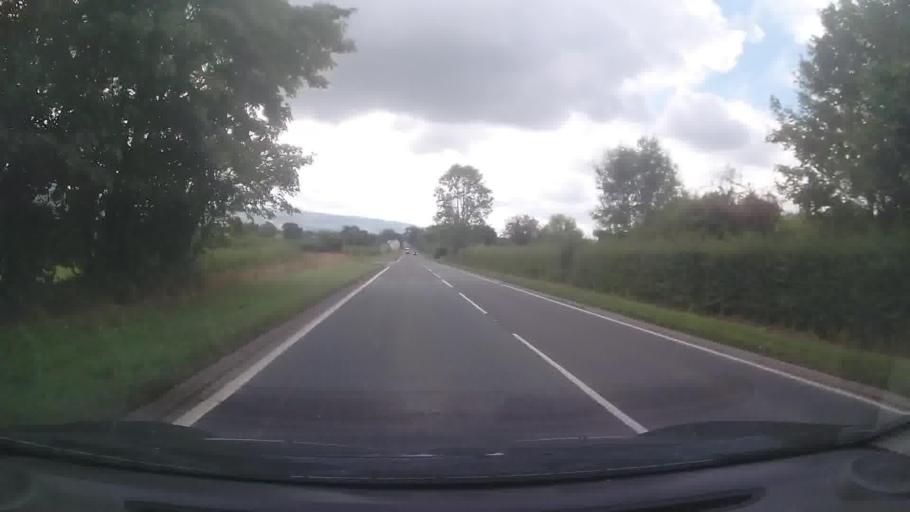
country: GB
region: England
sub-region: Shropshire
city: Pant
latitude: 52.7336
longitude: -3.0963
